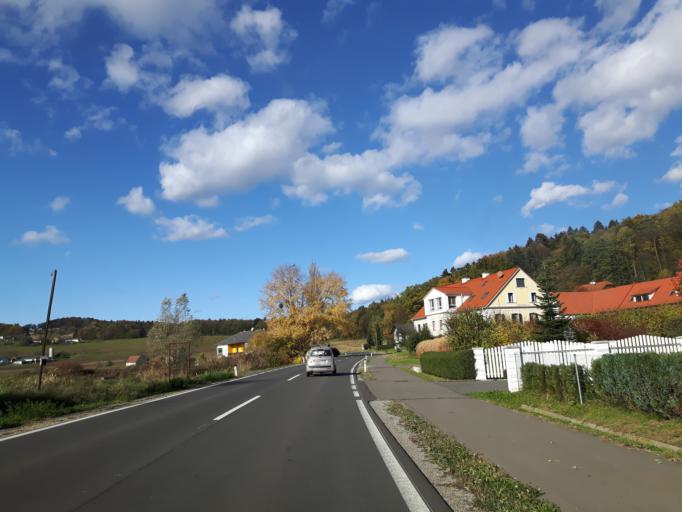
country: AT
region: Styria
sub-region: Politischer Bezirk Suedoststeiermark
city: Oberstorcha
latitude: 46.9509
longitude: 15.8313
